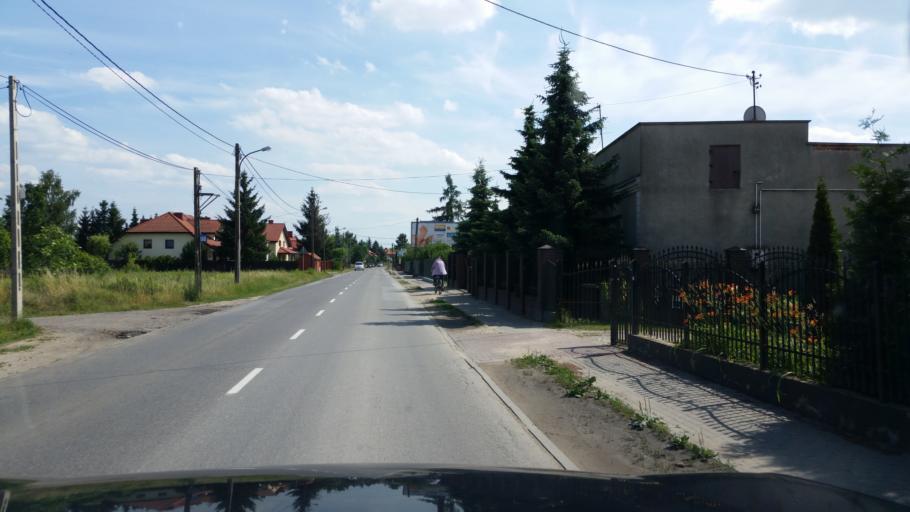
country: PL
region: Masovian Voivodeship
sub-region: Warszawa
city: Targowek
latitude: 52.3148
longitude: 21.0509
